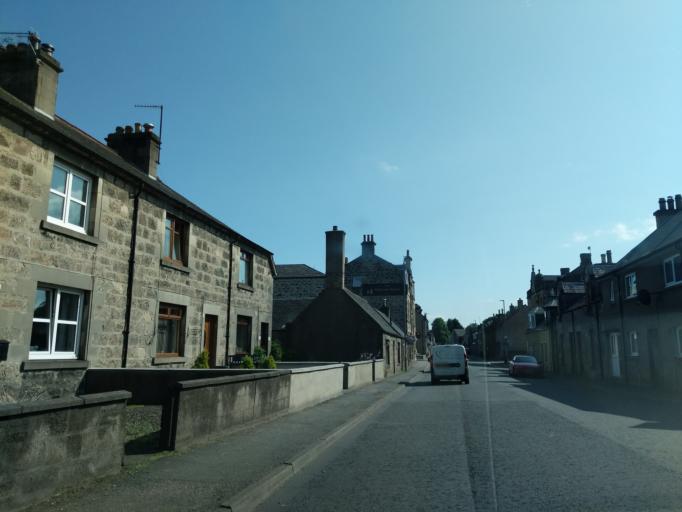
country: GB
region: Scotland
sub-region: Moray
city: Rothes
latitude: 57.5297
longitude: -3.2081
